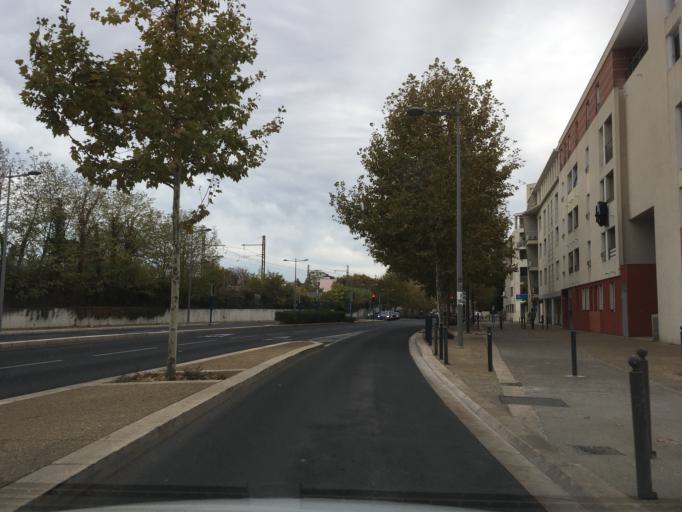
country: FR
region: Languedoc-Roussillon
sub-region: Departement de l'Herault
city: Montpellier
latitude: 43.6175
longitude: 3.8858
